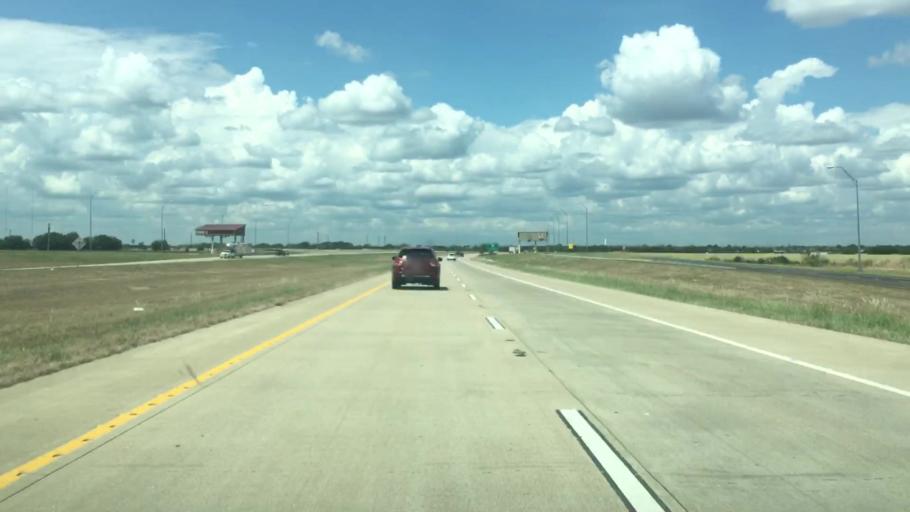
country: US
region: Texas
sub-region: Williamson County
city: Georgetown
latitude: 30.6225
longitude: -97.6180
